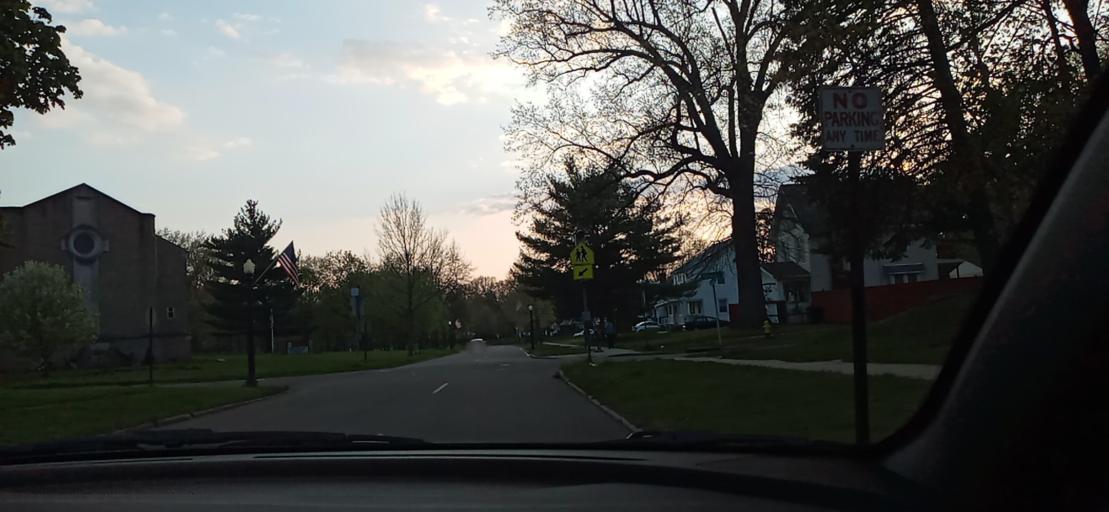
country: US
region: Ohio
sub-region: Summit County
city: Akron
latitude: 41.0442
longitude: -81.5162
